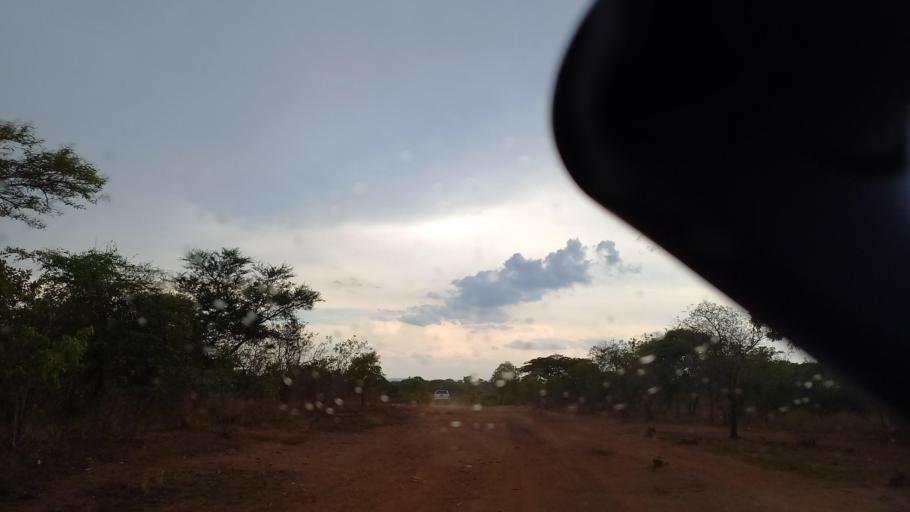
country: ZM
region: Lusaka
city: Kafue
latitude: -15.9844
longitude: 28.2635
